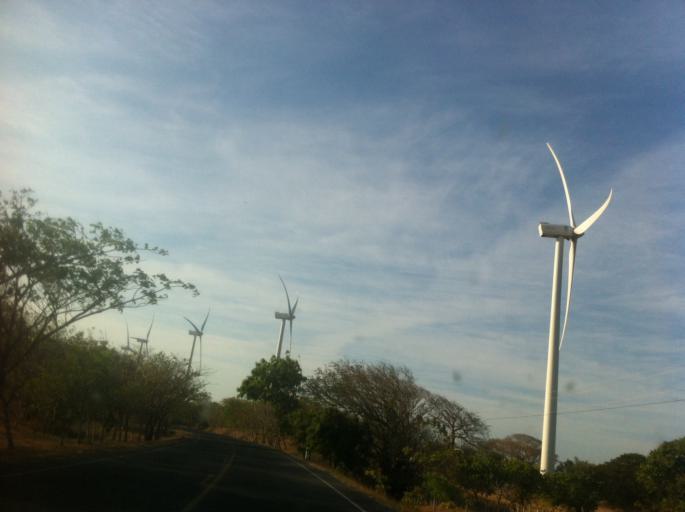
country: NI
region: Rivas
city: Rivas
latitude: 11.3306
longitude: -85.7218
